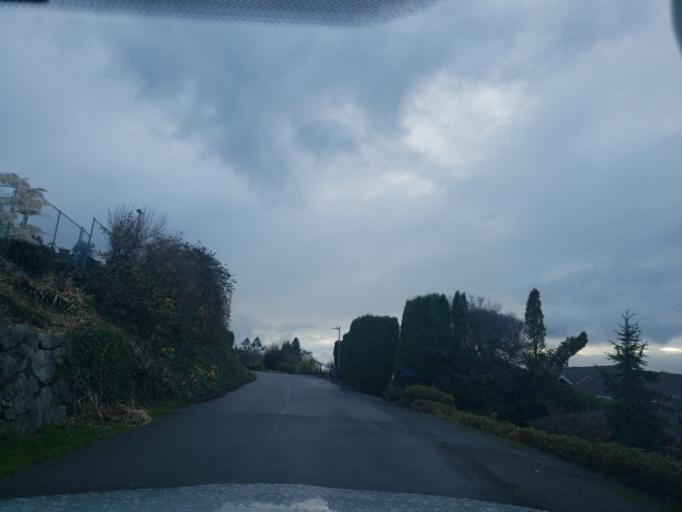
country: US
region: Washington
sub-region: King County
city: Shoreline
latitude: 47.7549
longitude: -122.3754
